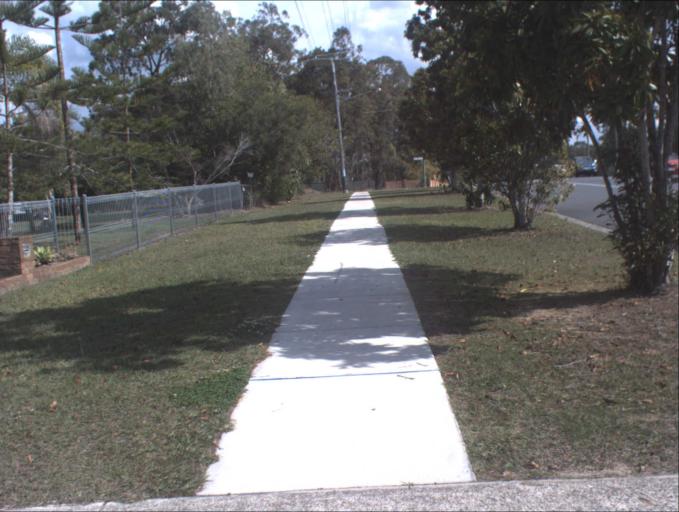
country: AU
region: Queensland
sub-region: Logan
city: Park Ridge South
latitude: -27.7018
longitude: 153.0102
